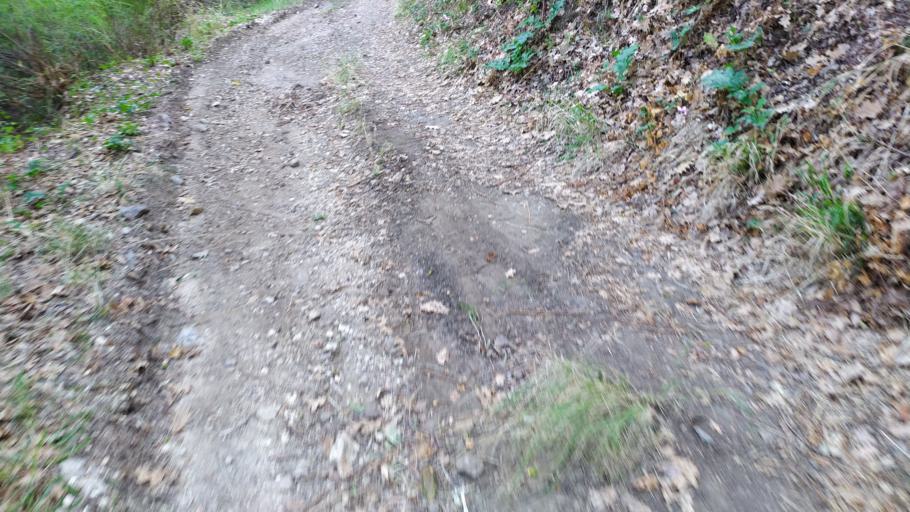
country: IT
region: Sicily
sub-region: Messina
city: Condro
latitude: 38.1632
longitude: 15.3308
